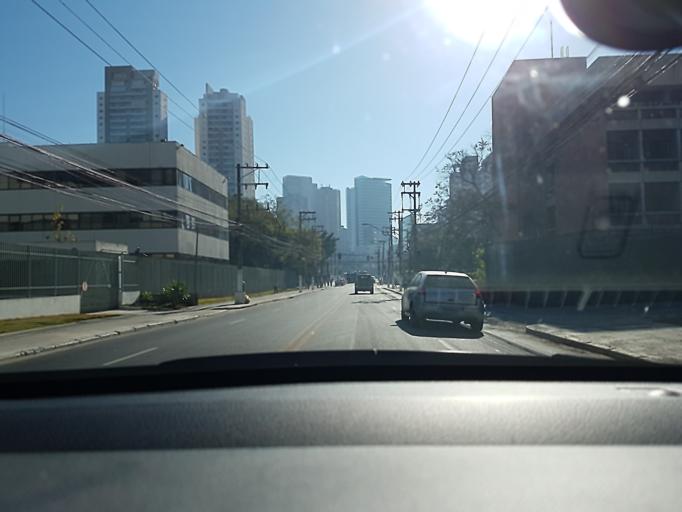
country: BR
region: Sao Paulo
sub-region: Taboao Da Serra
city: Taboao da Serra
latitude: -23.6303
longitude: -46.7093
